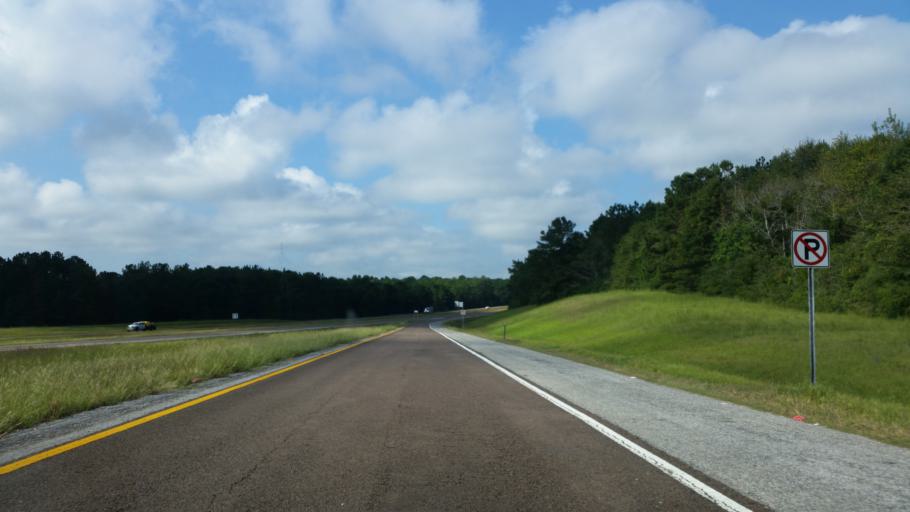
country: US
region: Alabama
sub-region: Baldwin County
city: Bay Minette
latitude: 30.9652
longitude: -87.7607
